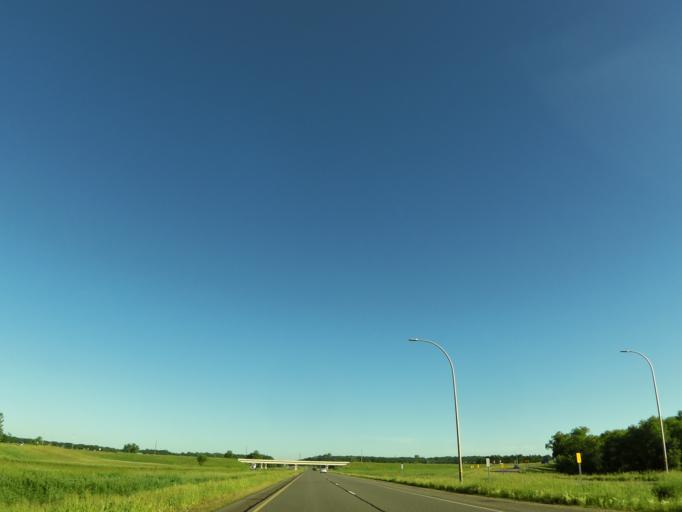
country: US
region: Minnesota
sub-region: Stearns County
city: Saint Joseph
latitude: 45.5122
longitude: -94.2803
